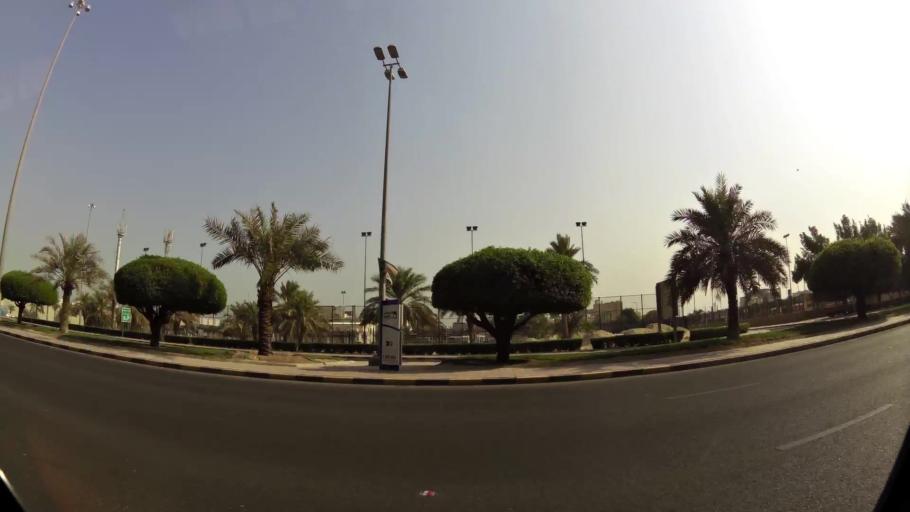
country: KW
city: Bayan
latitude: 29.3032
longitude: 48.0592
